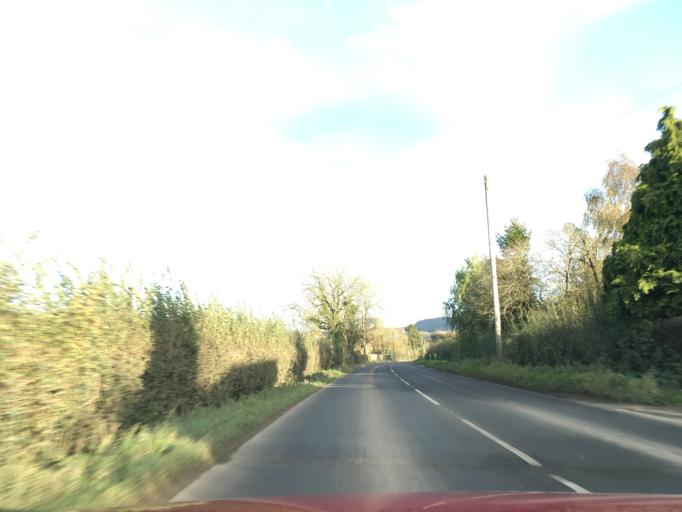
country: GB
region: England
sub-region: Gloucestershire
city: Berkeley
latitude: 51.6916
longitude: -2.4389
